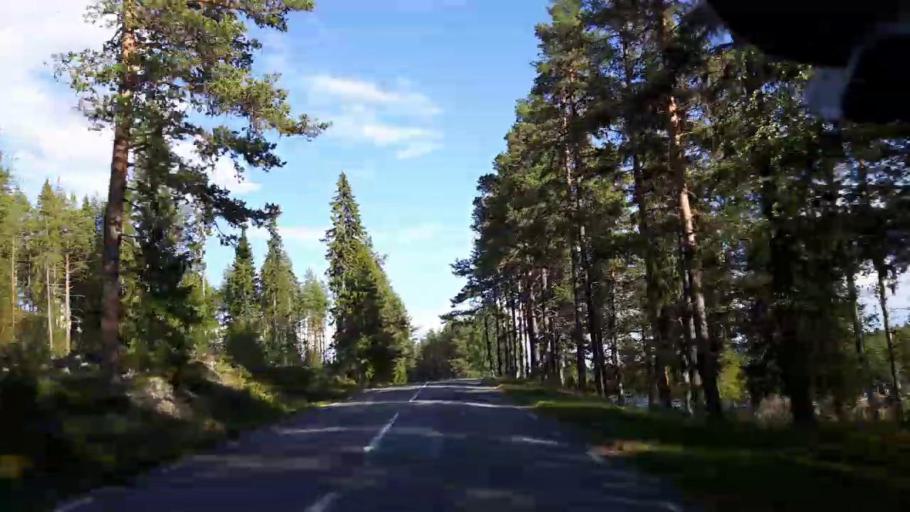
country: SE
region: Jaemtland
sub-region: Stroemsunds Kommun
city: Stroemsund
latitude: 63.3830
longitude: 15.5613
